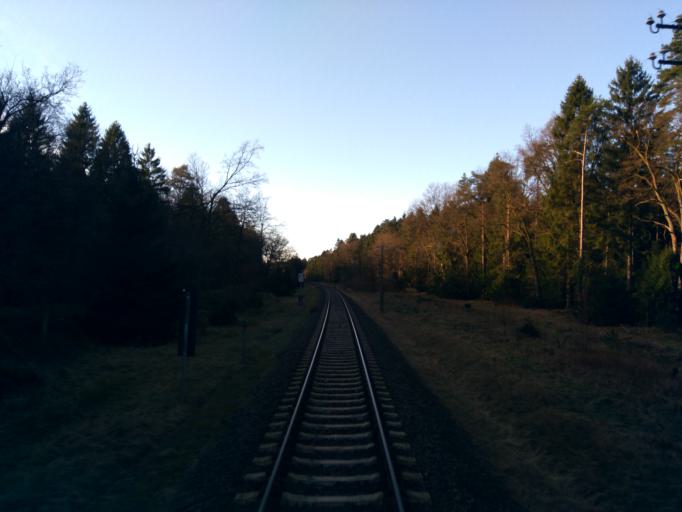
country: DE
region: Lower Saxony
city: Wietzendorf
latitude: 52.9977
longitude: 9.9581
